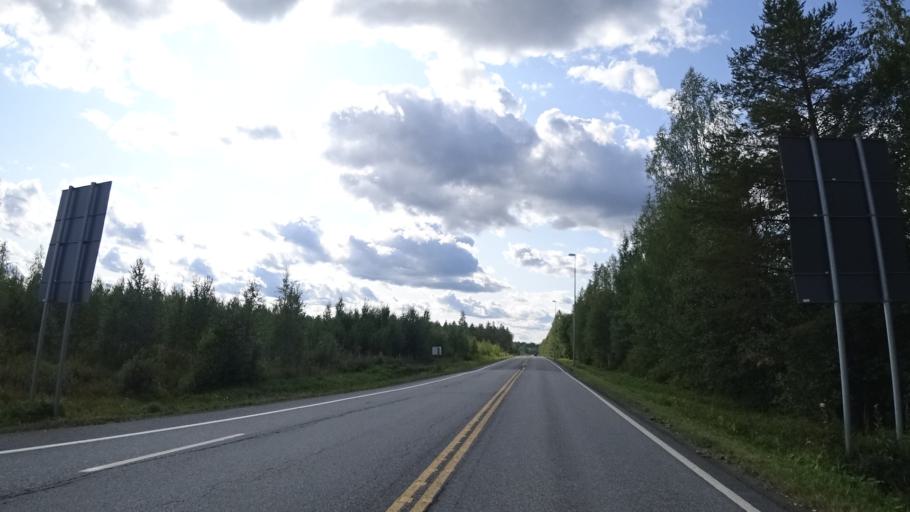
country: RU
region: Republic of Karelia
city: Vyartsilya
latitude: 62.1763
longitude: 30.5714
